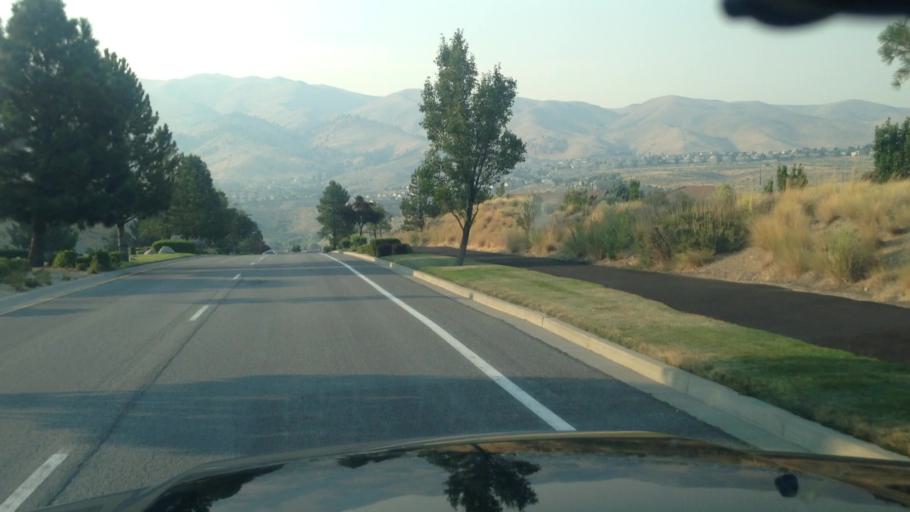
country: US
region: Nevada
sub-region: Washoe County
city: Mogul
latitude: 39.5249
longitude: -119.9113
